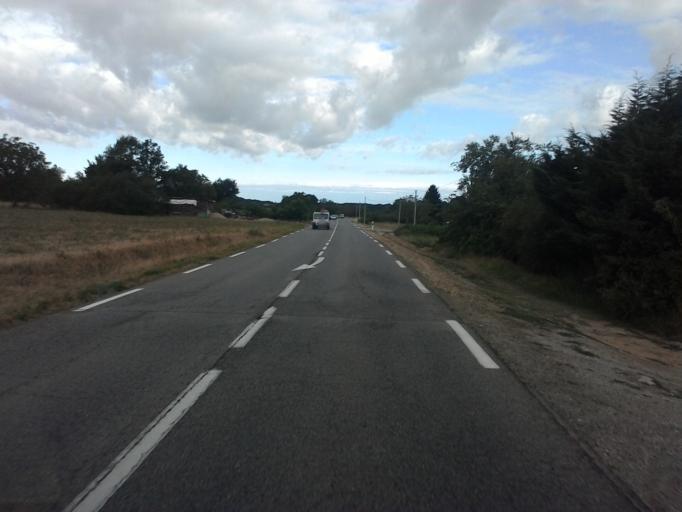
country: FR
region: Rhone-Alpes
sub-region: Departement de l'Ain
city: Saint-Sorlin-en-Bugey
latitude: 45.8748
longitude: 5.3593
